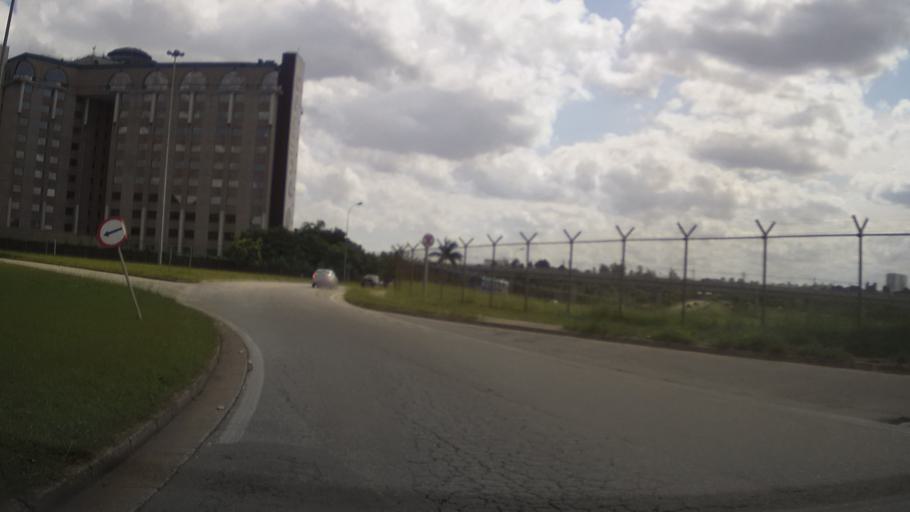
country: BR
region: Sao Paulo
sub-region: Guarulhos
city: Guarulhos
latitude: -23.4489
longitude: -46.4883
